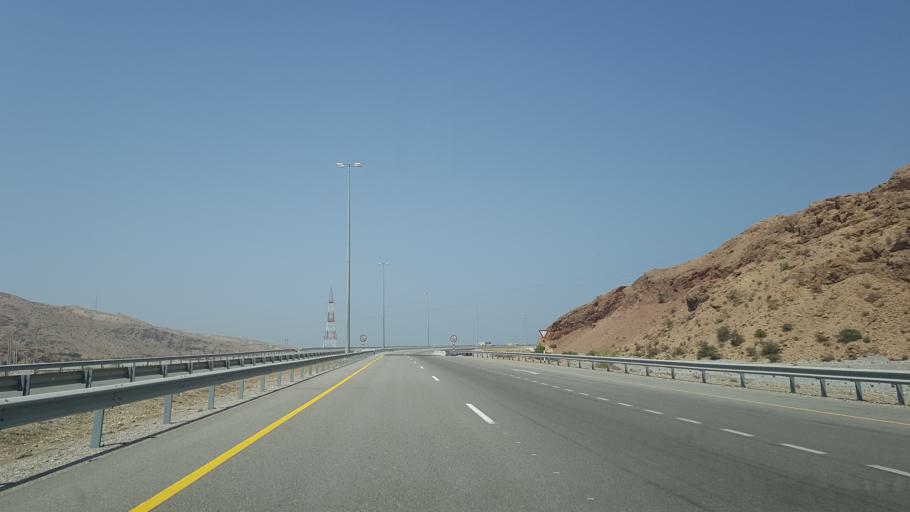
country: OM
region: Muhafazat Masqat
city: Muscat
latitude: 23.2039
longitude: 58.8821
